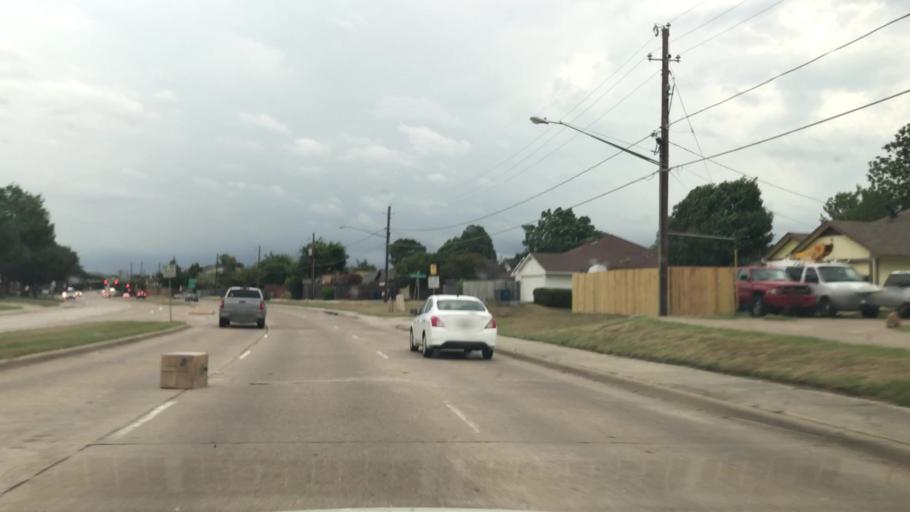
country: US
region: Texas
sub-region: Dallas County
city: Carrollton
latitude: 32.9969
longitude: -96.8722
